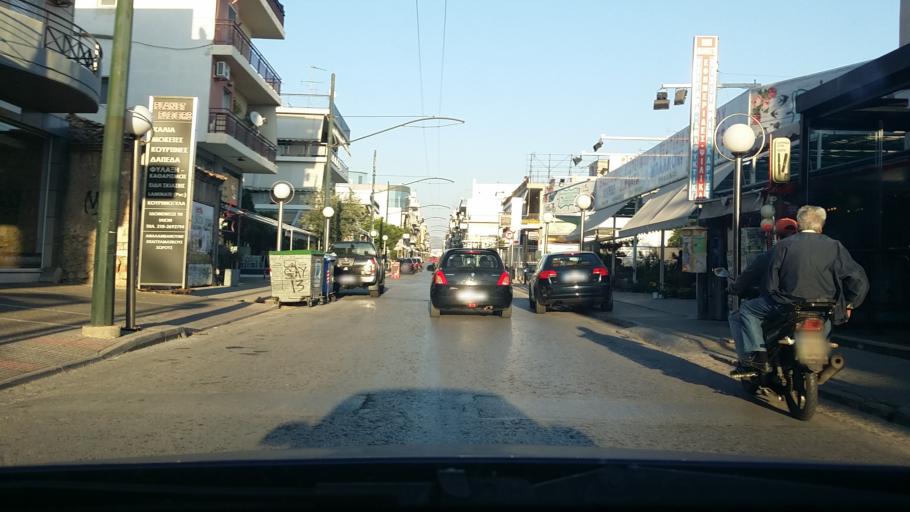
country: GR
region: Attica
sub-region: Nomarchia Athinas
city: Ilion
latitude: 38.0307
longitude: 23.7035
